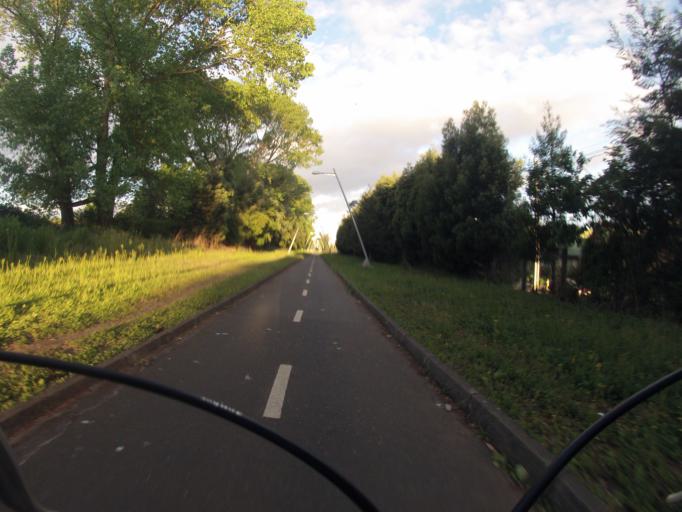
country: CL
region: Araucania
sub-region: Provincia de Cautin
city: Temuco
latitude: -38.7536
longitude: -72.6557
